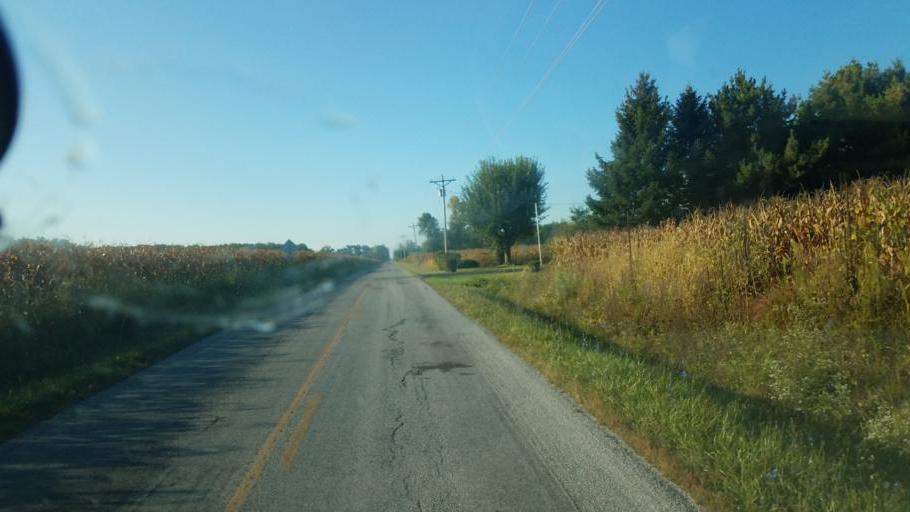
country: US
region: Ohio
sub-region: Morrow County
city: Cardington
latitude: 40.5558
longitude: -82.9957
